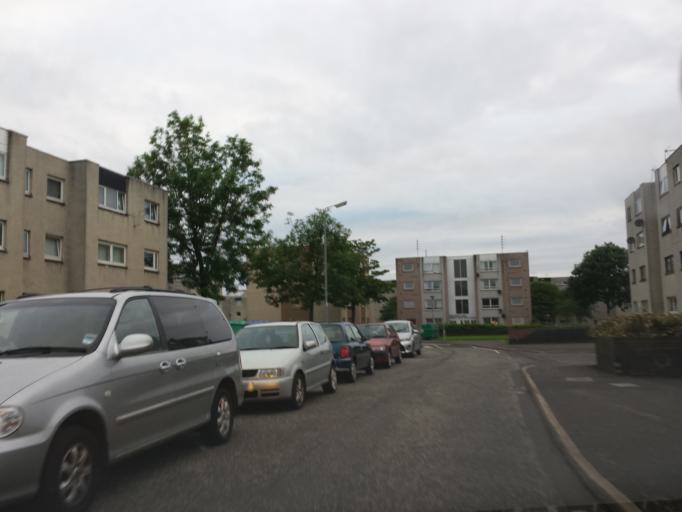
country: GB
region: Scotland
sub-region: South Ayrshire
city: Ayr
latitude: 55.4693
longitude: -4.6244
